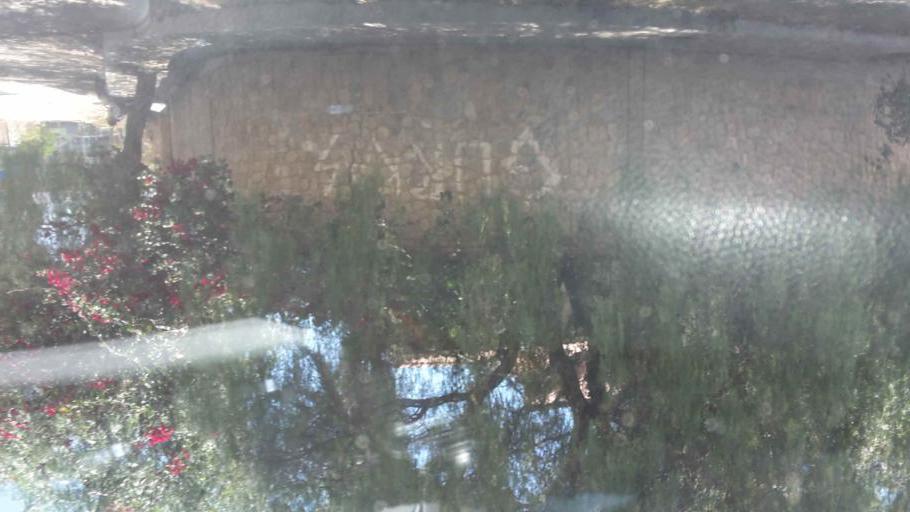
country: BO
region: Cochabamba
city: Cochabamba
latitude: -17.3415
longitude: -66.2174
